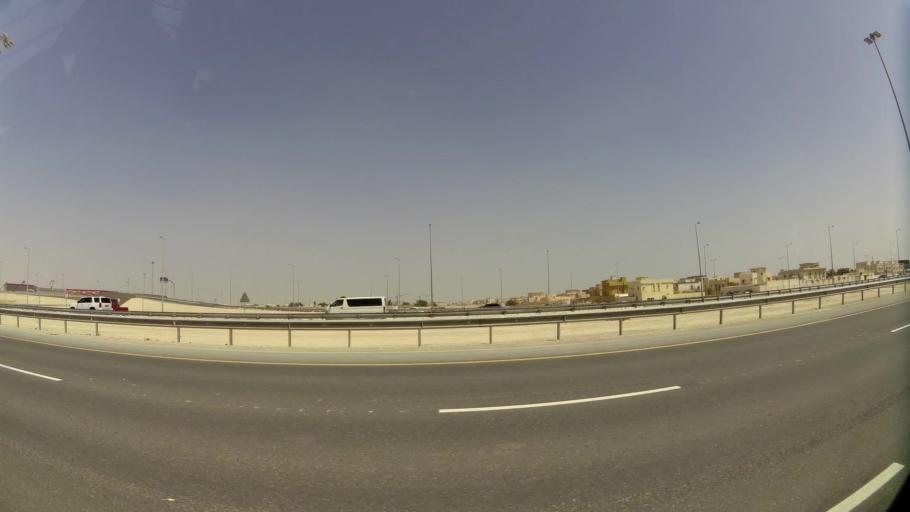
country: QA
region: Baladiyat Umm Salal
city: Umm Salal Muhammad
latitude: 25.3766
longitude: 51.4416
